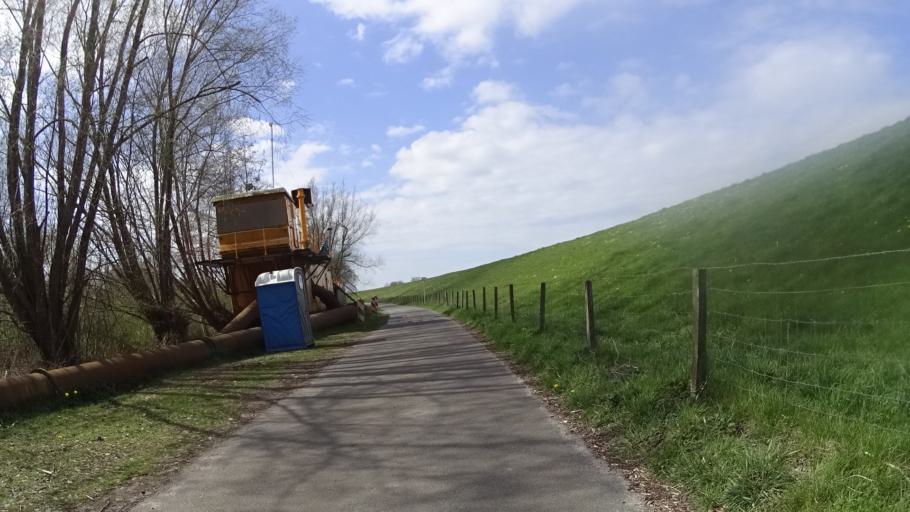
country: DE
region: Lower Saxony
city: Weener
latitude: 53.1037
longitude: 7.3251
